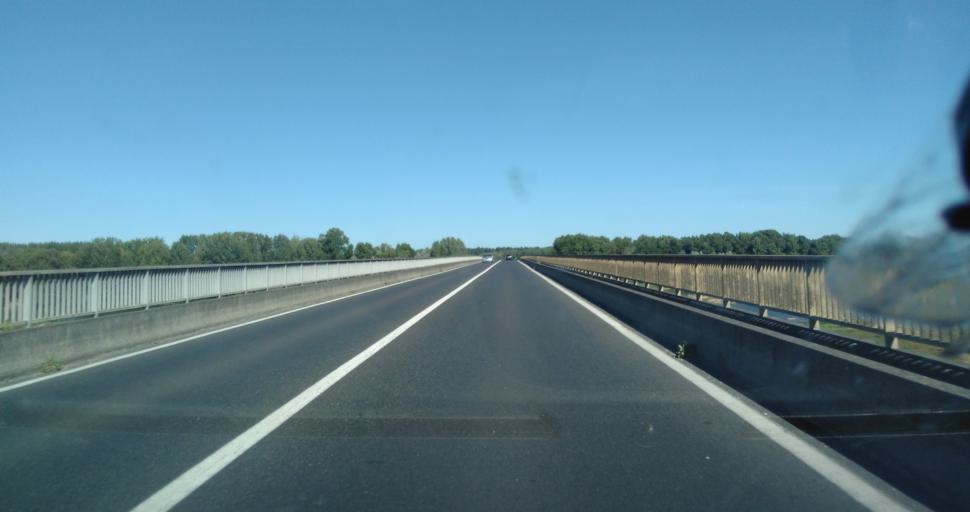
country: FR
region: Centre
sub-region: Departement d'Indre-et-Loire
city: Charge
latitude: 47.4261
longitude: 1.0110
